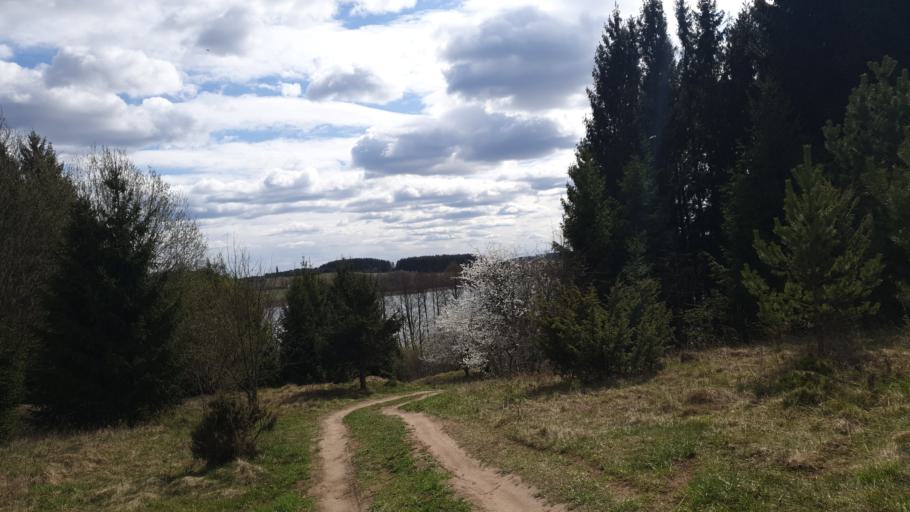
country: LT
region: Vilnius County
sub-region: Trakai
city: Rudiskes
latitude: 54.5094
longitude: 24.6833
